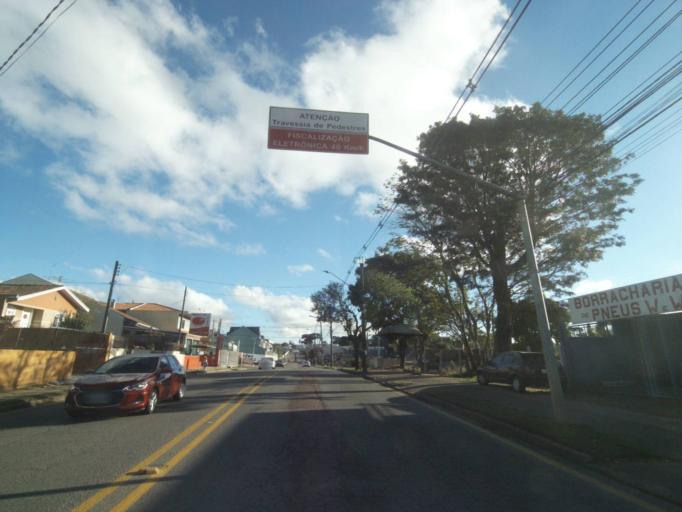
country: BR
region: Parana
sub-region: Sao Jose Dos Pinhais
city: Sao Jose dos Pinhais
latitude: -25.5284
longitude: -49.2926
